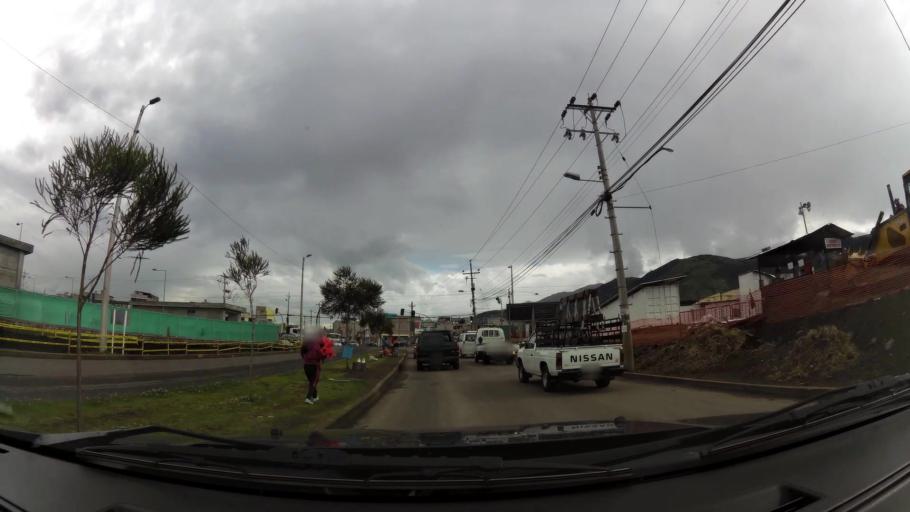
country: EC
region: Pichincha
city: Quito
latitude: -0.3004
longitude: -78.5562
